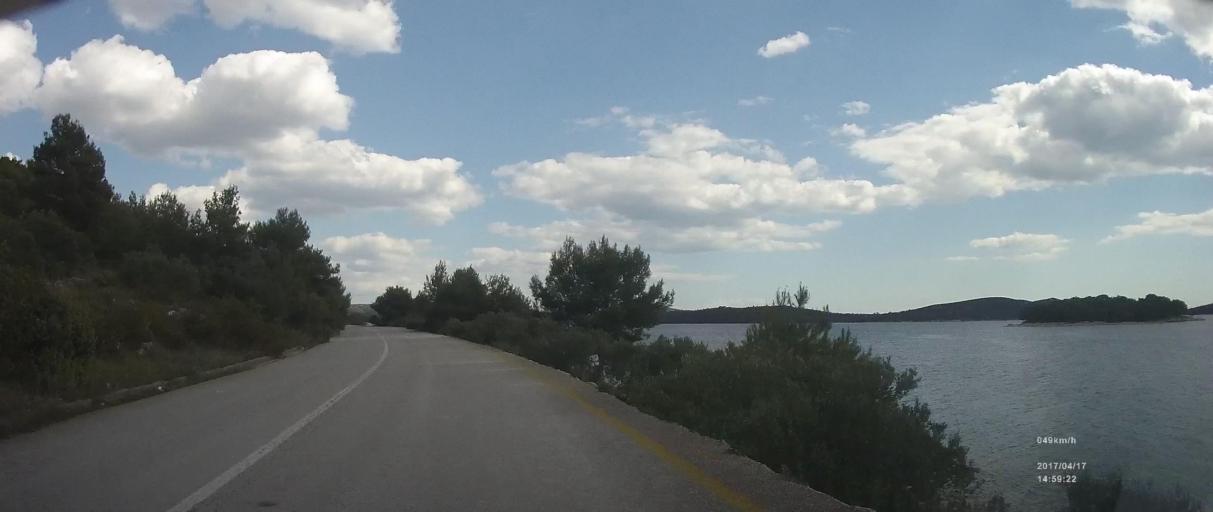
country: HR
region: Sibensko-Kniniska
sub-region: Grad Sibenik
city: Tisno
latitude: 43.8342
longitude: 15.6332
